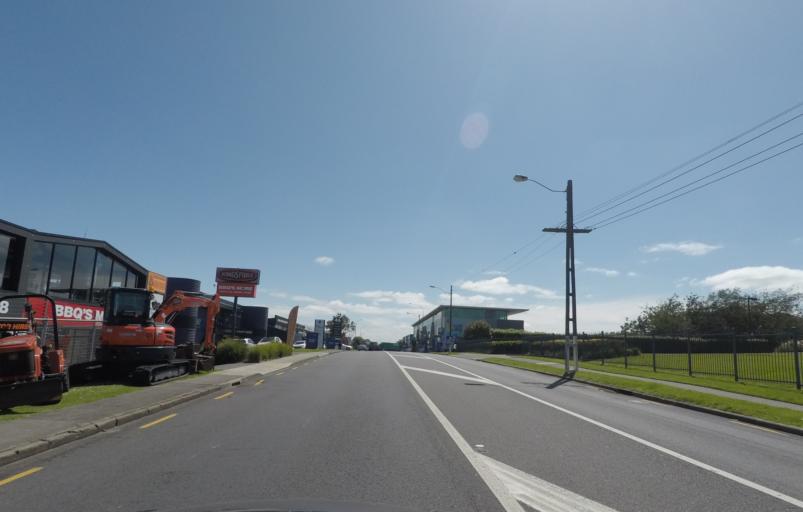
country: NZ
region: Auckland
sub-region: Auckland
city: Tamaki
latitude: -36.8932
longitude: 174.8383
